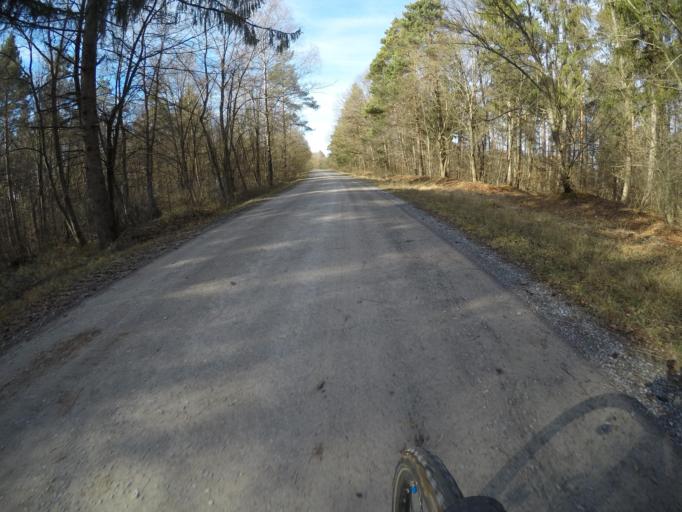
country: DE
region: Baden-Wuerttemberg
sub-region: Regierungsbezirk Stuttgart
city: Schonaich
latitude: 48.6900
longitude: 9.0738
